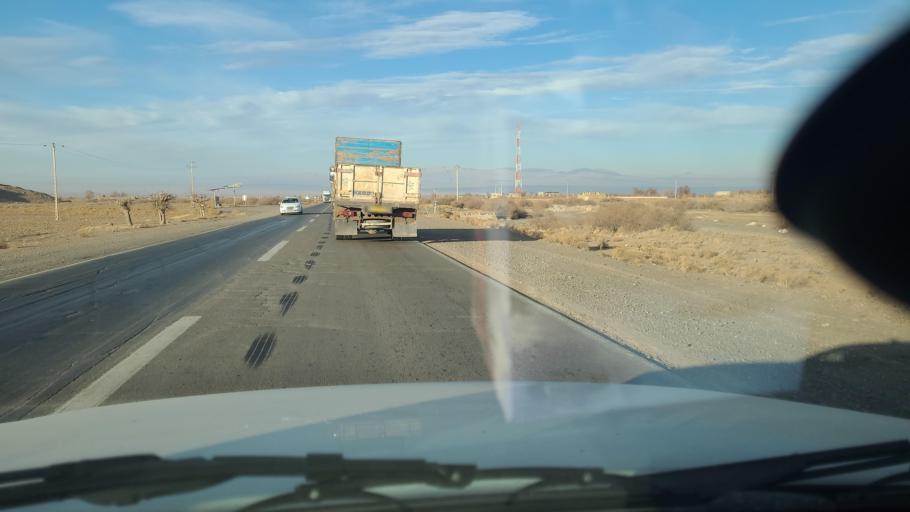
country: IR
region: Razavi Khorasan
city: Neqab
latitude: 36.4864
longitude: 57.5310
